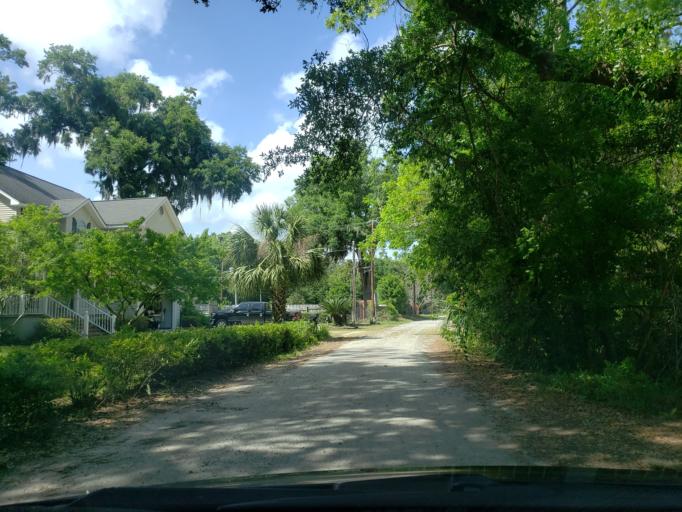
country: US
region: Georgia
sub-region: Chatham County
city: Thunderbolt
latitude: 32.0185
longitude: -81.0620
